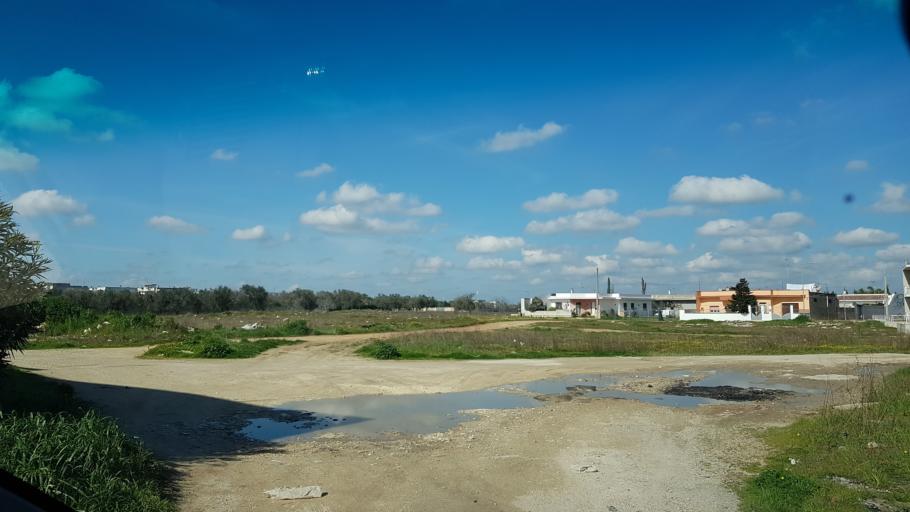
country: IT
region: Apulia
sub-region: Provincia di Lecce
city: Veglie
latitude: 40.3402
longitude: 17.9600
